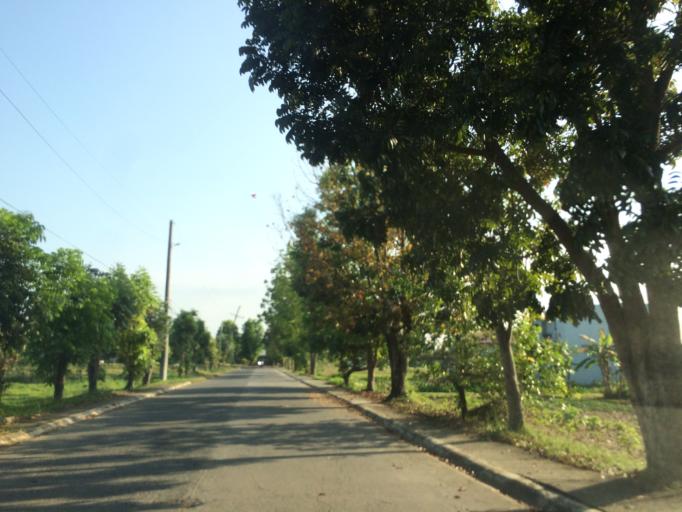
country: PH
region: Calabarzon
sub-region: Province of Rizal
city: San Mateo
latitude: 14.6745
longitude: 121.1225
